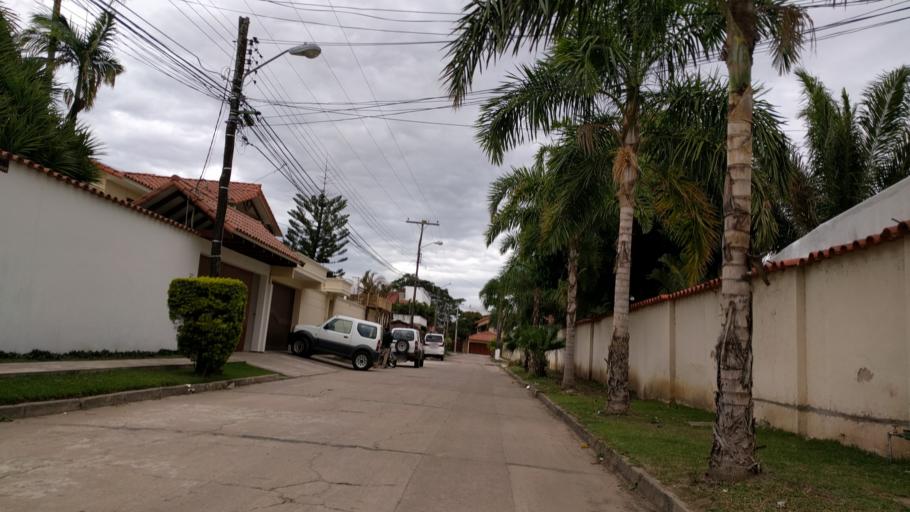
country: BO
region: Santa Cruz
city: Santa Cruz de la Sierra
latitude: -17.8054
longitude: -63.2102
